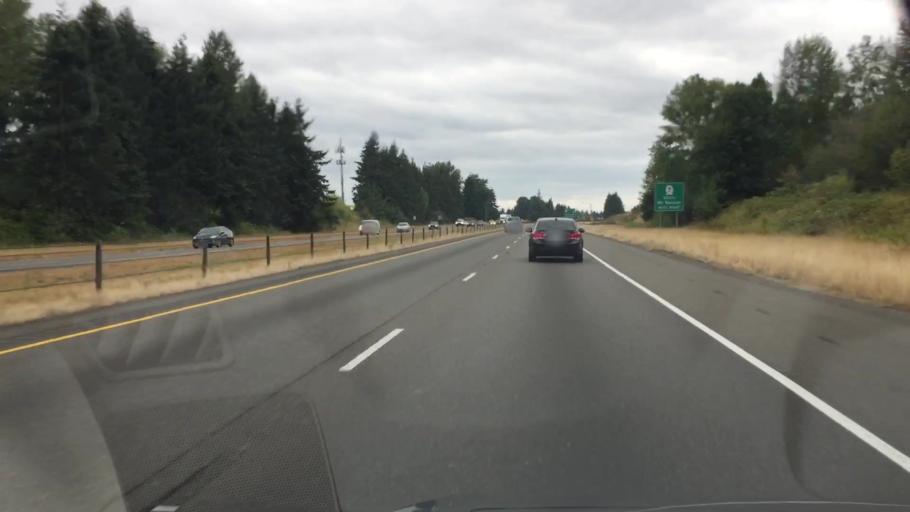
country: US
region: Washington
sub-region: Pierce County
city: Parkland
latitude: 47.1586
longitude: -122.4236
